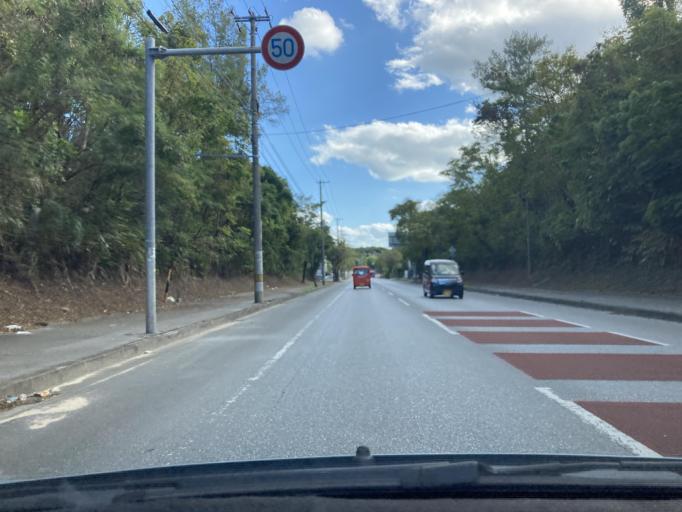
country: JP
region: Okinawa
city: Gushikawa
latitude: 26.3717
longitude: 127.8289
